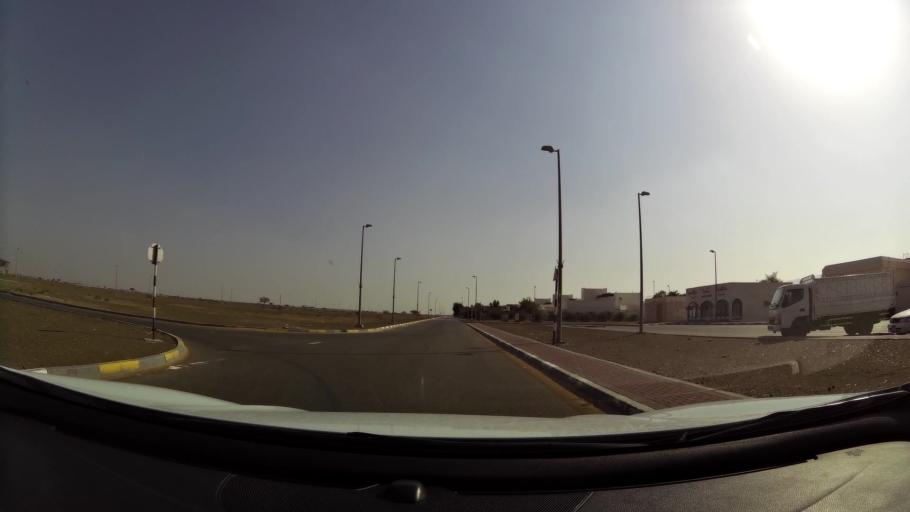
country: AE
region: Abu Dhabi
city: Al Ain
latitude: 24.0757
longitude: 55.8730
